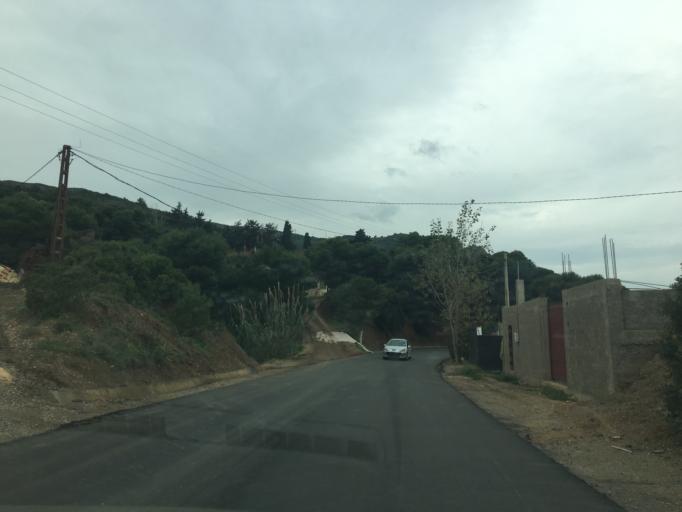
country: DZ
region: Tipaza
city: Tipasa
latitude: 36.6399
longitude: 2.3386
